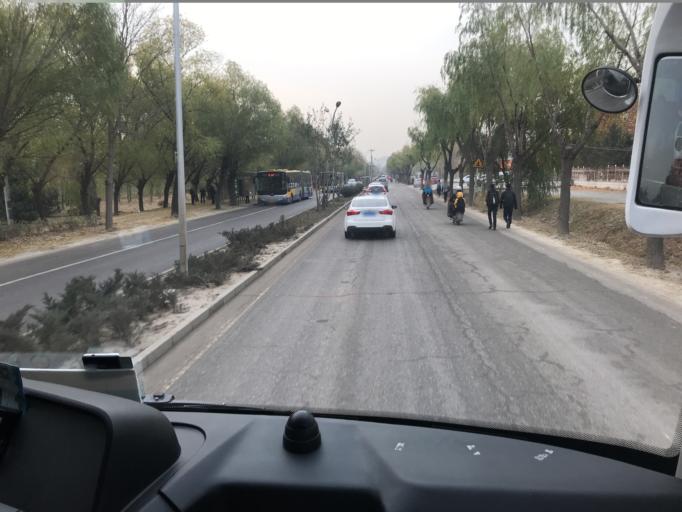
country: CN
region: Beijing
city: Wenquan
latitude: 40.0897
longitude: 116.2098
